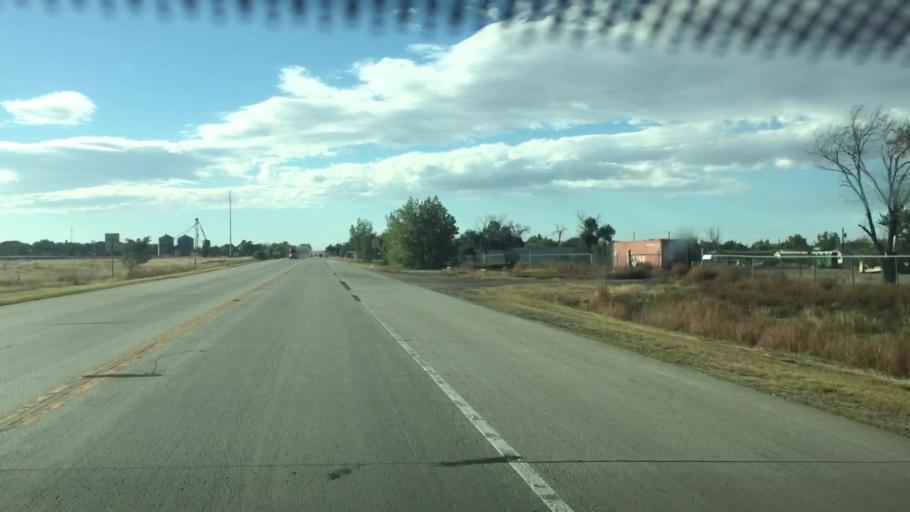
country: US
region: Colorado
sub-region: Lincoln County
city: Hugo
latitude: 39.1302
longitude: -103.4573
